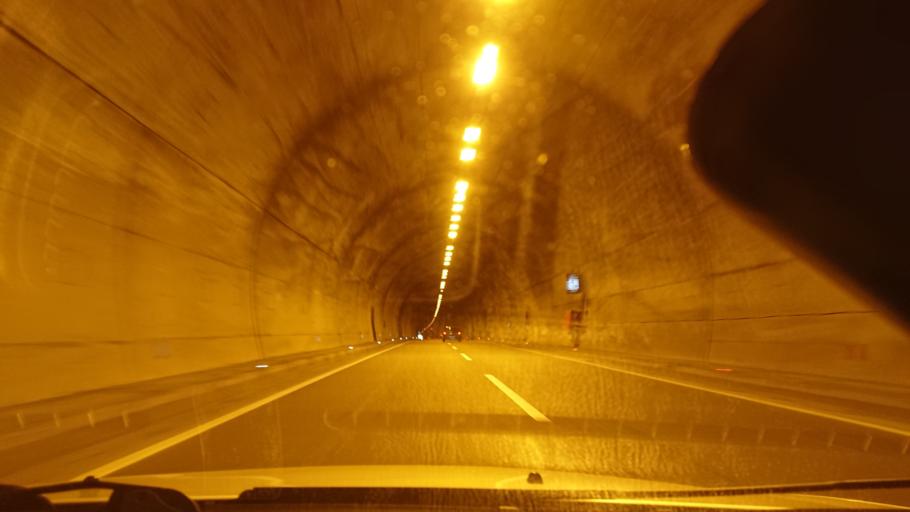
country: TR
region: Trabzon
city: Espiye
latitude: 40.9694
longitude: 38.6313
